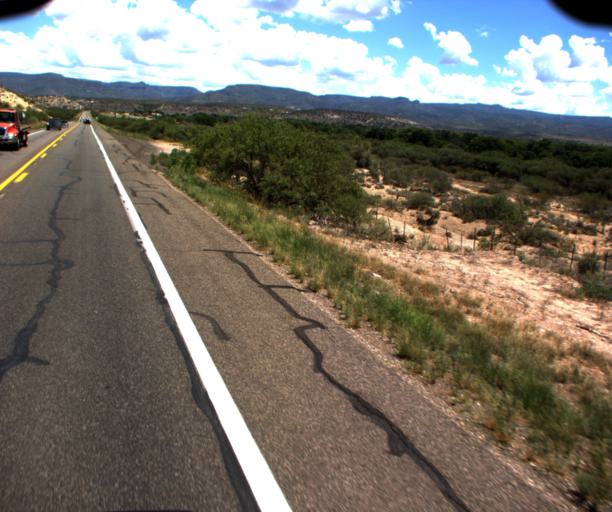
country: US
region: Arizona
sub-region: Yavapai County
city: Camp Verde
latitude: 34.5274
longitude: -111.8009
